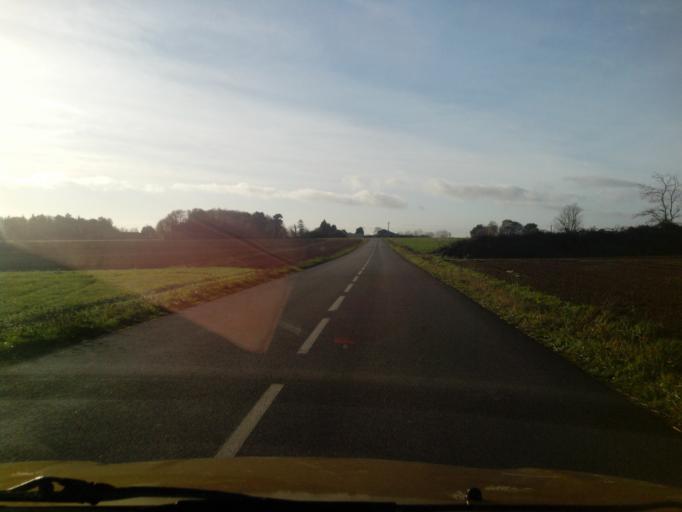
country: FR
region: Brittany
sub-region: Departement du Morbihan
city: Meneac
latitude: 48.1065
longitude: -2.4554
